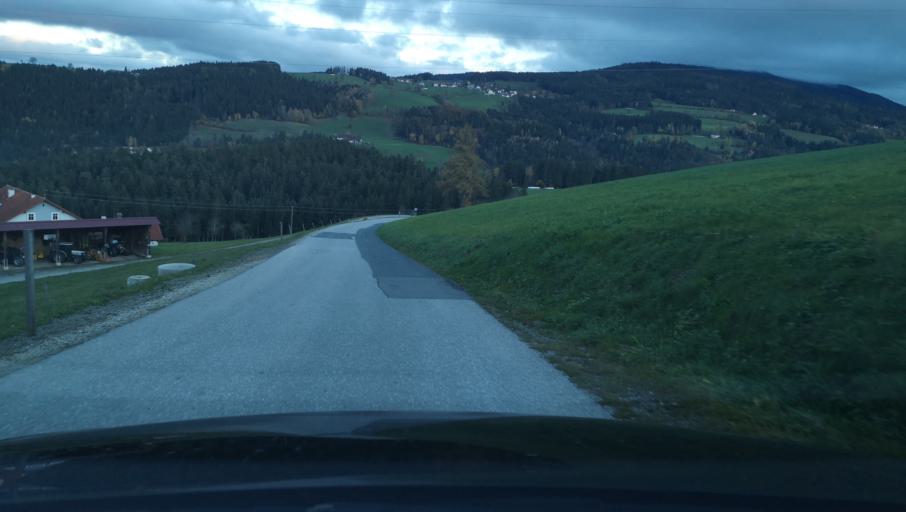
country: AT
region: Styria
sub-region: Politischer Bezirk Weiz
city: Koglhof
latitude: 47.3293
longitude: 15.6823
